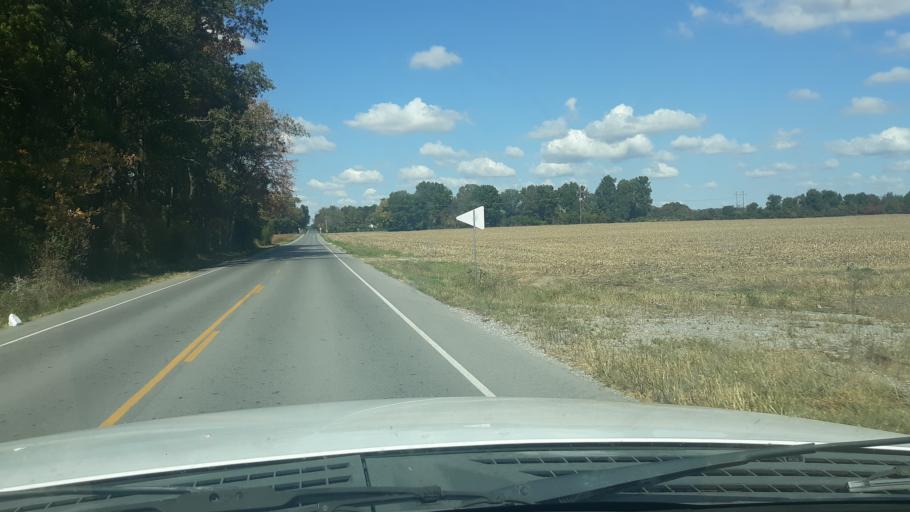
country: US
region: Illinois
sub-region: Saline County
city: Eldorado
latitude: 37.8081
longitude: -88.4848
